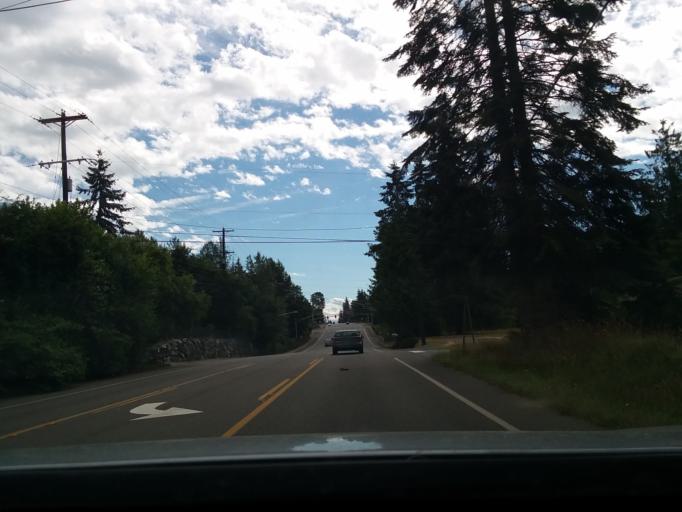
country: US
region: Washington
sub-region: Snohomish County
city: West Lake Stevens
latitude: 47.9780
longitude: -122.1125
